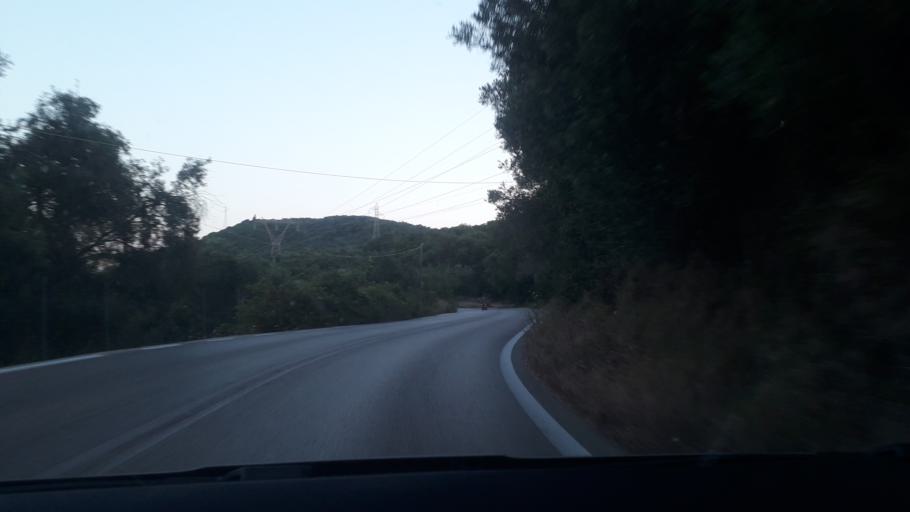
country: GR
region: Ionian Islands
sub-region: Nomos Kerkyras
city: Agios Matthaios
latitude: 39.4515
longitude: 19.9267
